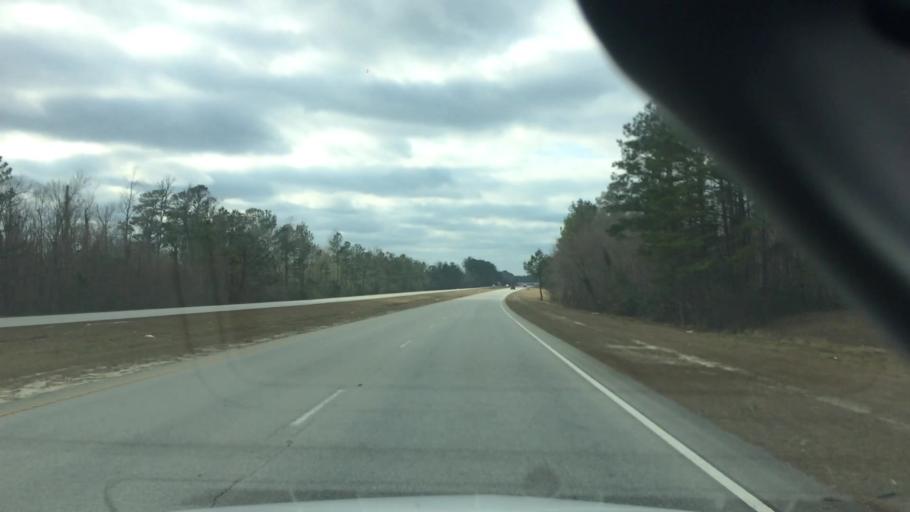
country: US
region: North Carolina
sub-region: Brunswick County
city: Bolivia
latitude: 34.0678
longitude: -78.1799
